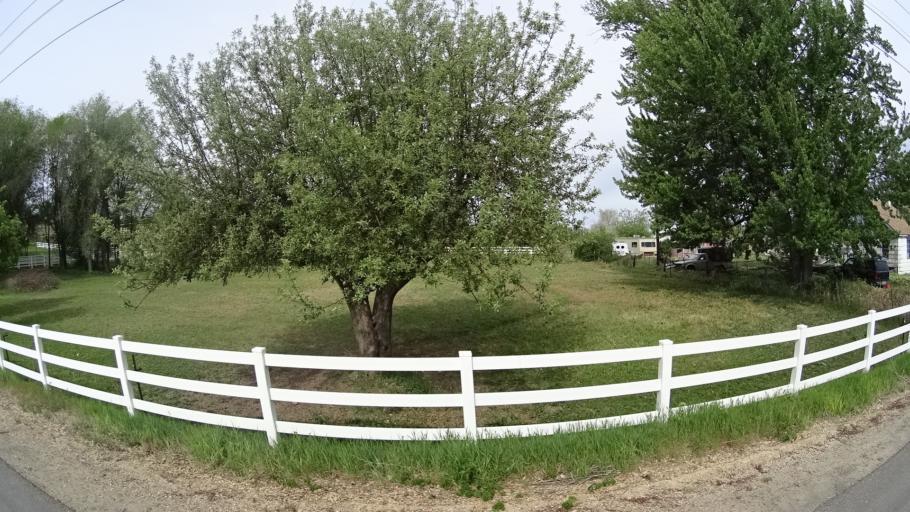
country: US
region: Idaho
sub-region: Ada County
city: Meridian
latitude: 43.5368
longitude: -116.3145
